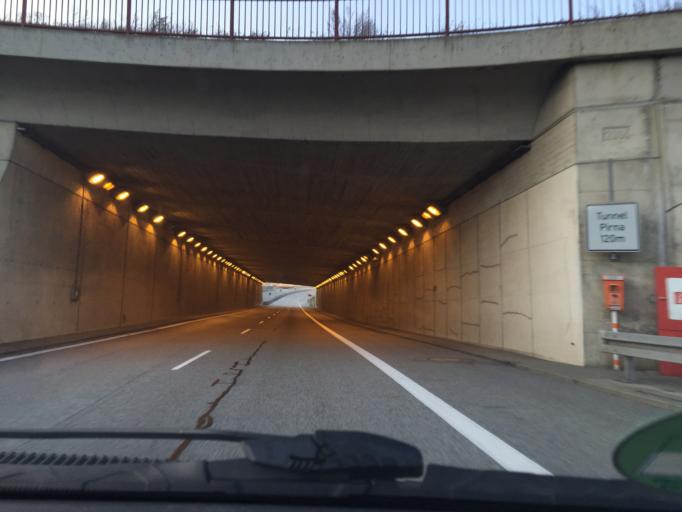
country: DE
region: Saxony
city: Pirna
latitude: 50.9529
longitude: 13.9222
